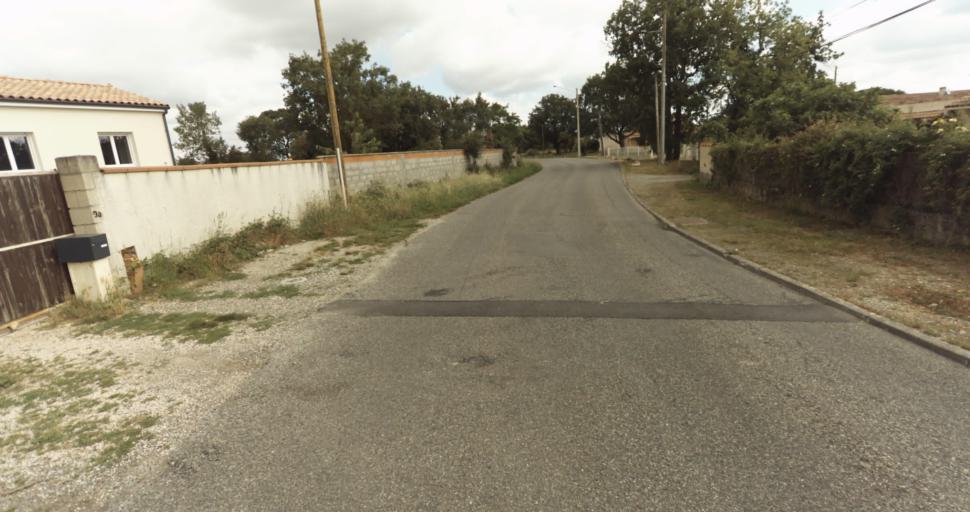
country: FR
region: Midi-Pyrenees
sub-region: Departement de la Haute-Garonne
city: Fonsorbes
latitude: 43.5529
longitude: 1.2272
